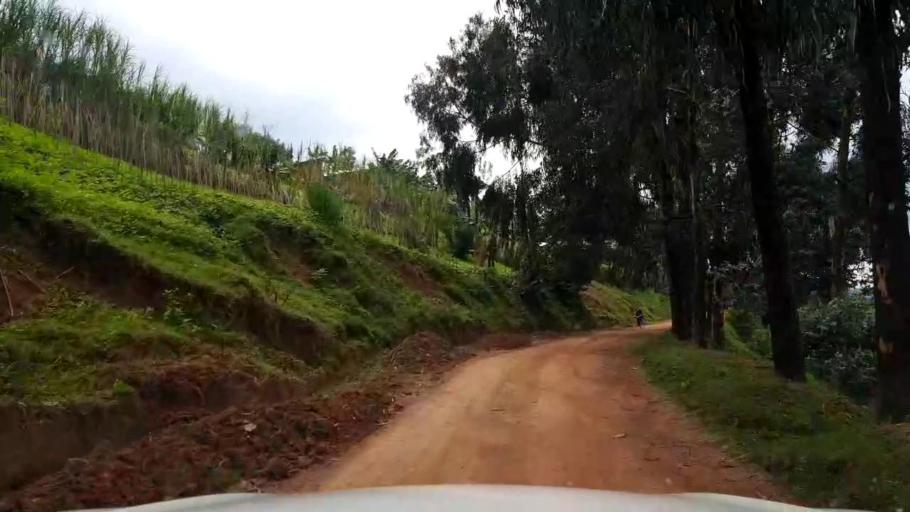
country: UG
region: Western Region
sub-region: Kabale District
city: Kabale
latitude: -1.4308
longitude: 29.8668
